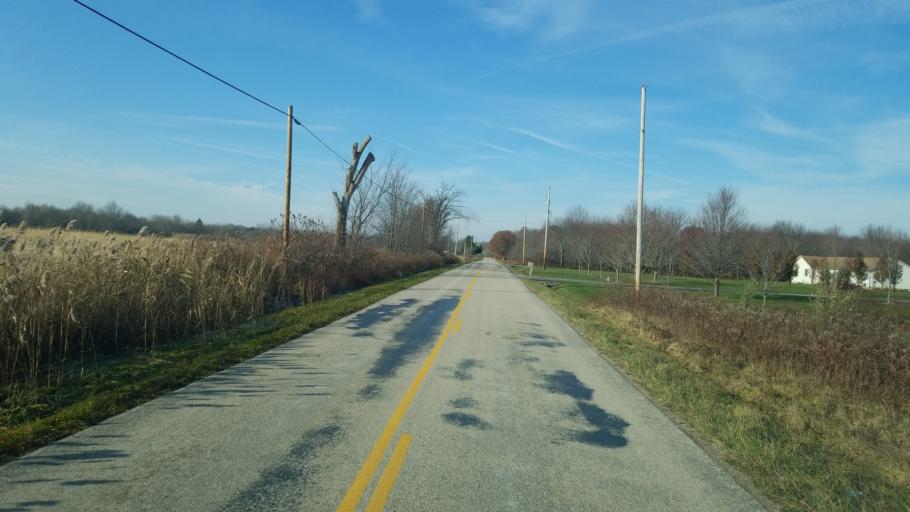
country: US
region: Ohio
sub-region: Ashtabula County
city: North Kingsville
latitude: 41.8245
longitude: -80.6889
